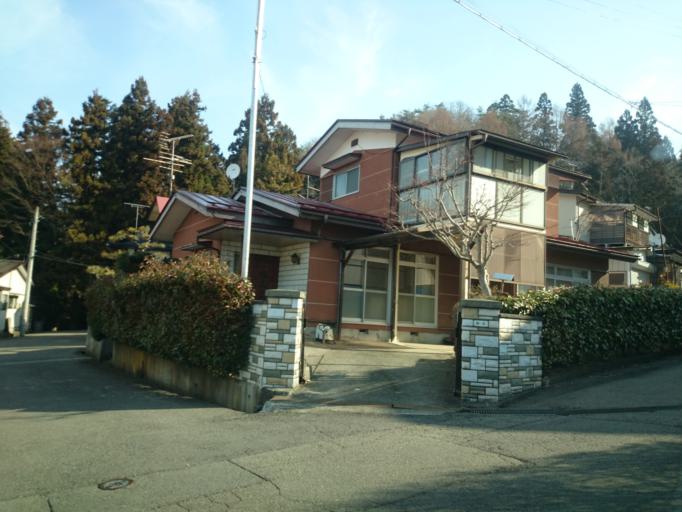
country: JP
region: Fukushima
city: Kitakata
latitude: 37.4940
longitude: 139.9515
